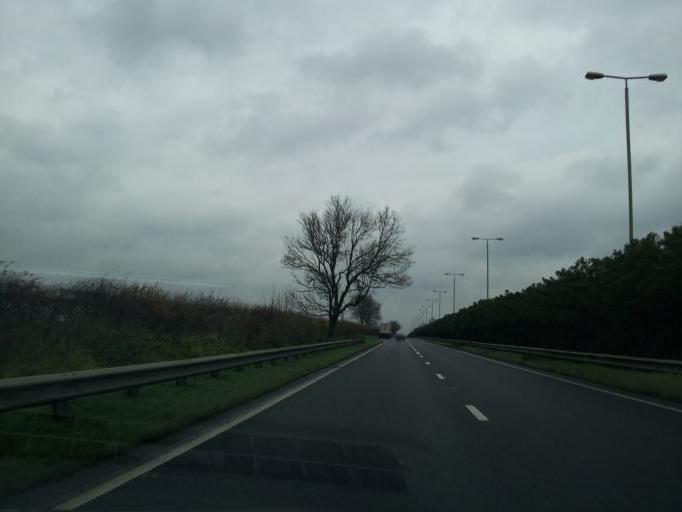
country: GB
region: England
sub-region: Leicestershire
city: Queniborough
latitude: 52.7475
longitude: -1.0628
